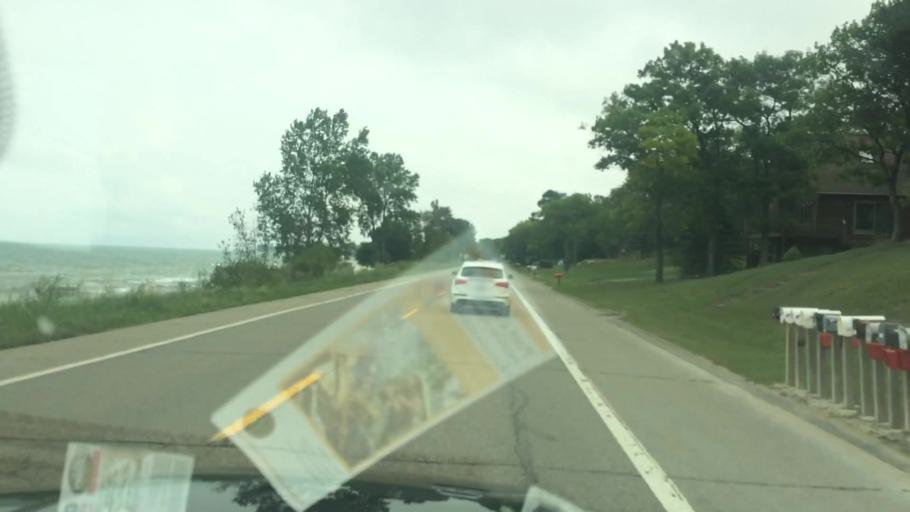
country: US
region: Michigan
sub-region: Huron County
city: Pigeon
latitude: 43.9875
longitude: -83.1507
